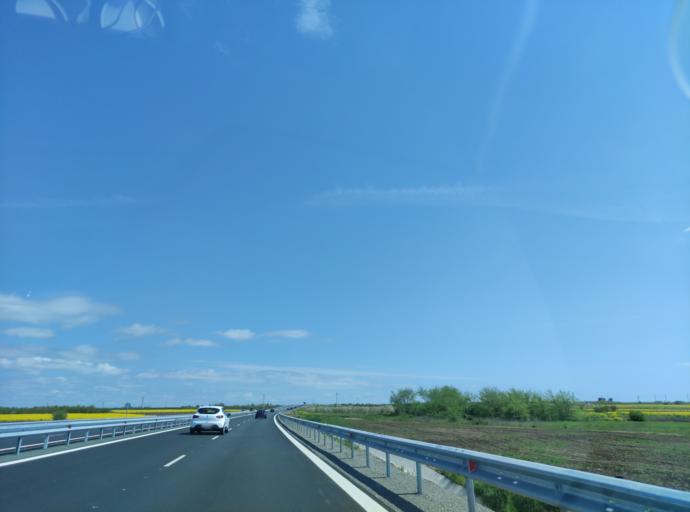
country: BG
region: Burgas
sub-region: Obshtina Pomorie
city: Pomorie
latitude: 42.5741
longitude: 27.5757
